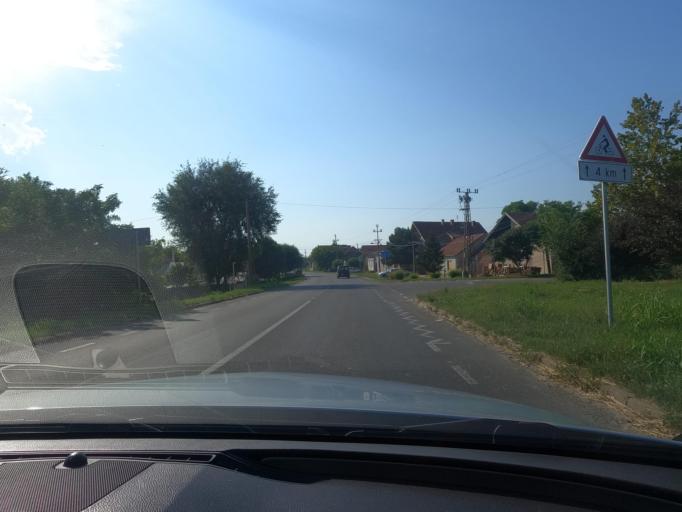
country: RS
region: Autonomna Pokrajina Vojvodina
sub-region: Juznobacki Okrug
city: Kovilj
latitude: 45.2929
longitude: 19.9587
